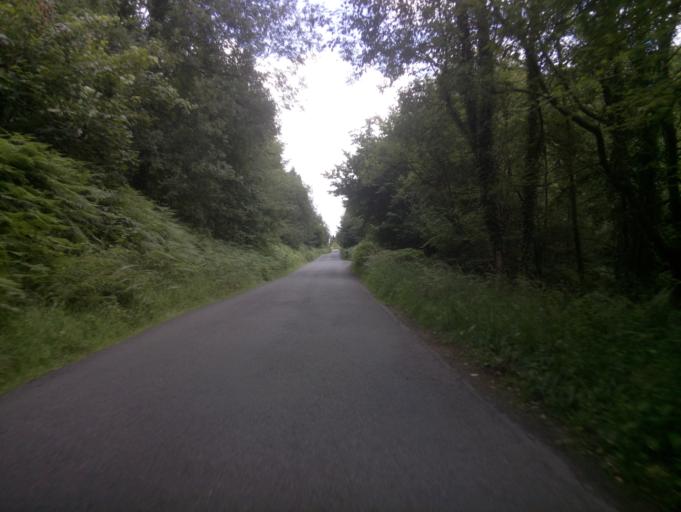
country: GB
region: England
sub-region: Gloucestershire
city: Cinderford
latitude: 51.8067
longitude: -2.4900
